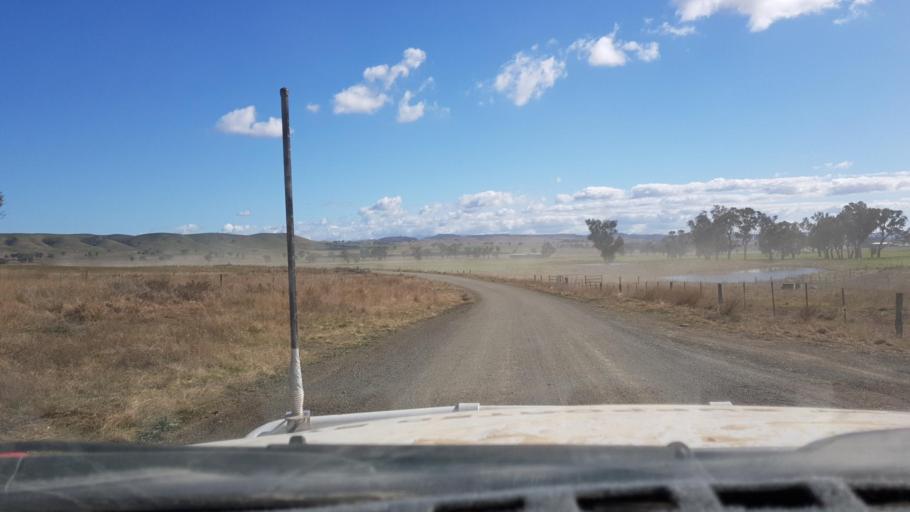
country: AU
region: New South Wales
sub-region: Narrabri
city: Blair Athol
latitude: -30.5369
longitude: 150.4482
